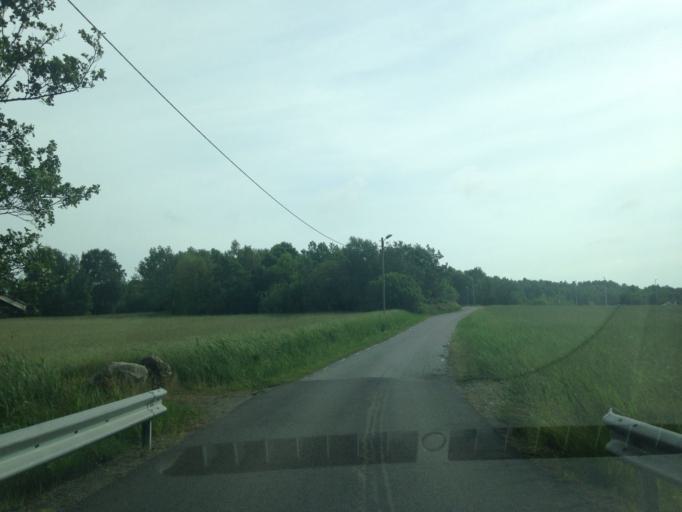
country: SE
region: Vaestra Goetaland
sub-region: Goteborg
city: Majorna
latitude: 57.7532
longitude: 11.8675
